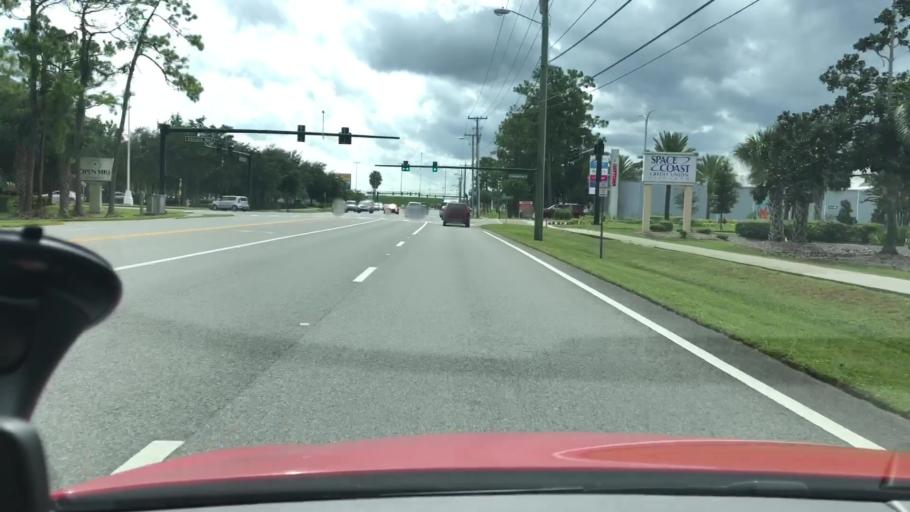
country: US
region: Florida
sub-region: Volusia County
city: Daytona Beach
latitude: 29.1958
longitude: -81.0684
